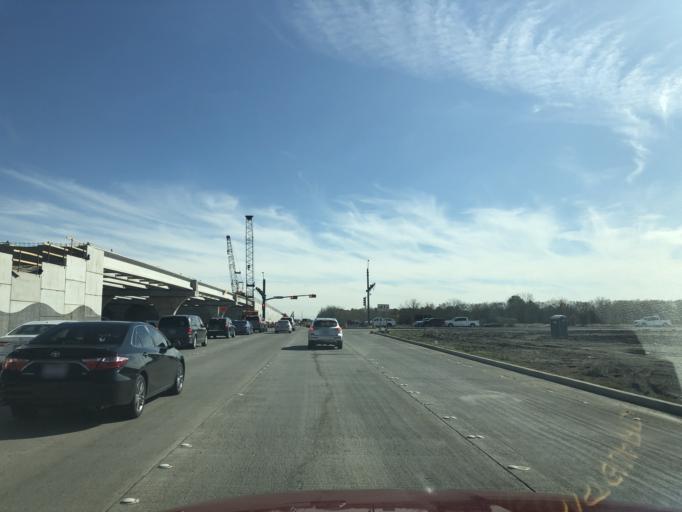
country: US
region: Texas
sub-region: Galveston County
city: Dickinson
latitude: 29.4665
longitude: -95.0916
